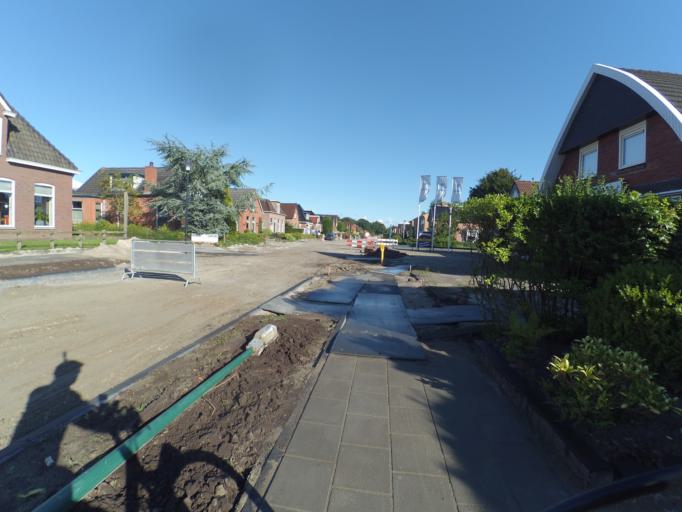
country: NL
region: Friesland
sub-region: Gemeente Achtkarspelen
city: Buitenpost
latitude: 53.2573
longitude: 6.1406
